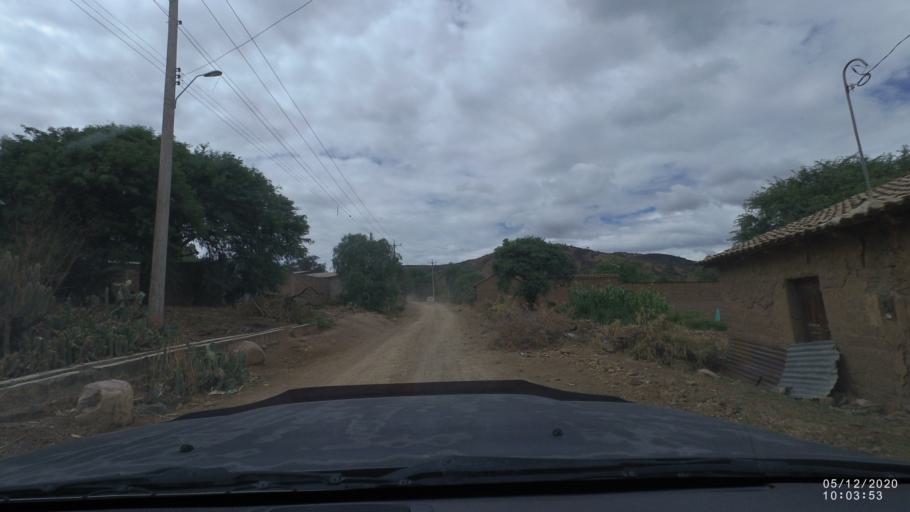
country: BO
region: Cochabamba
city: Sipe Sipe
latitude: -17.4599
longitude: -66.2869
